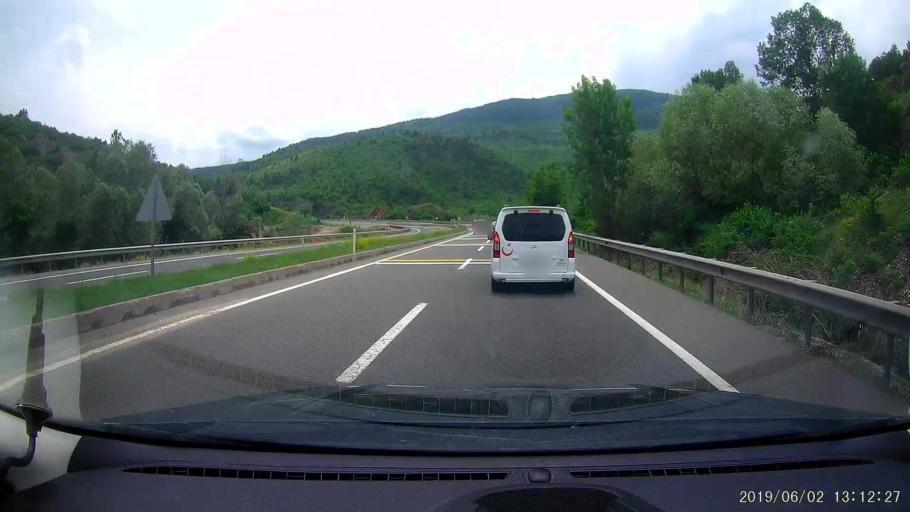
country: TR
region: Karabuk
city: Gozyeri
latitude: 40.8600
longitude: 32.6358
